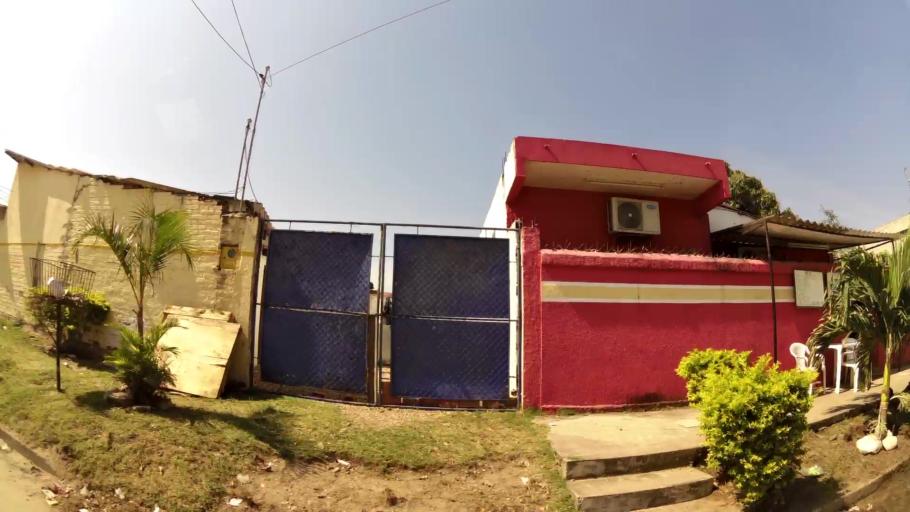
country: BO
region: Santa Cruz
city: Santa Cruz de la Sierra
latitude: -17.7455
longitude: -63.1795
